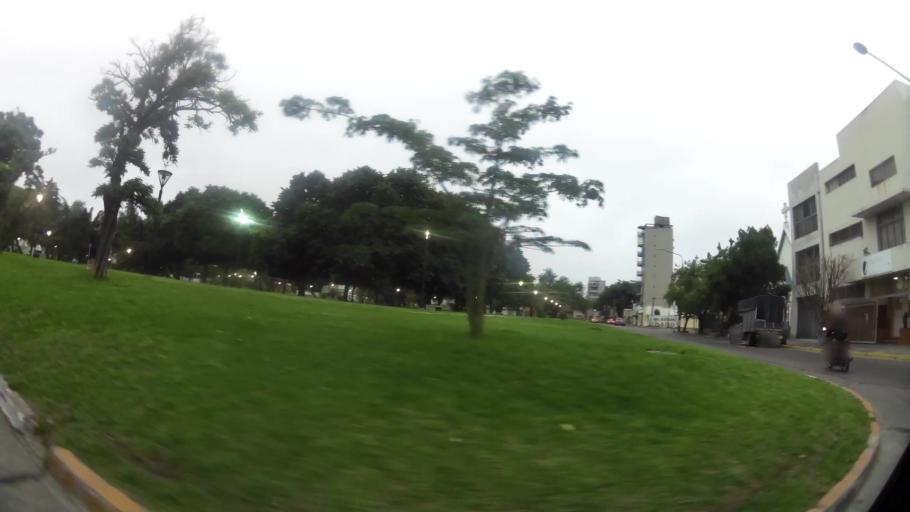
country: AR
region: Buenos Aires
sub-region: Partido de La Plata
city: La Plata
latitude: -34.9169
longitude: -57.9755
